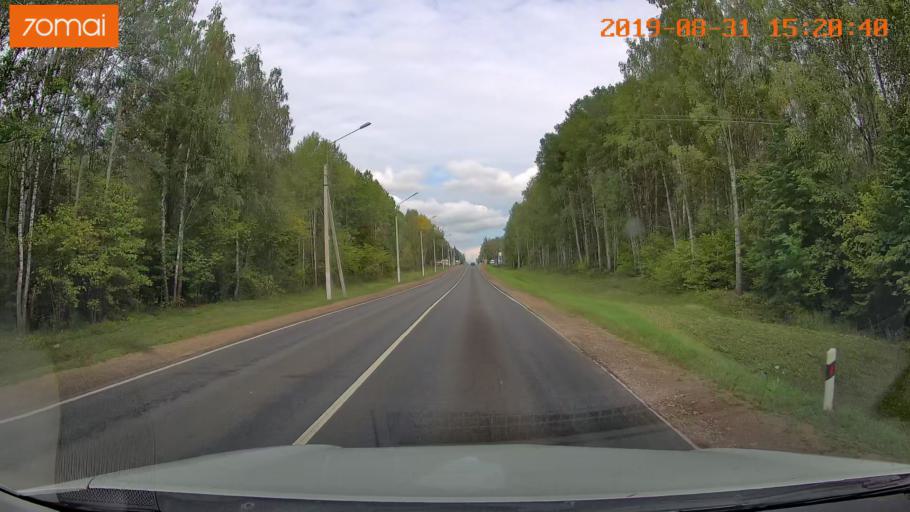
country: RU
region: Kaluga
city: Baryatino
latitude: 54.4915
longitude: 34.4402
